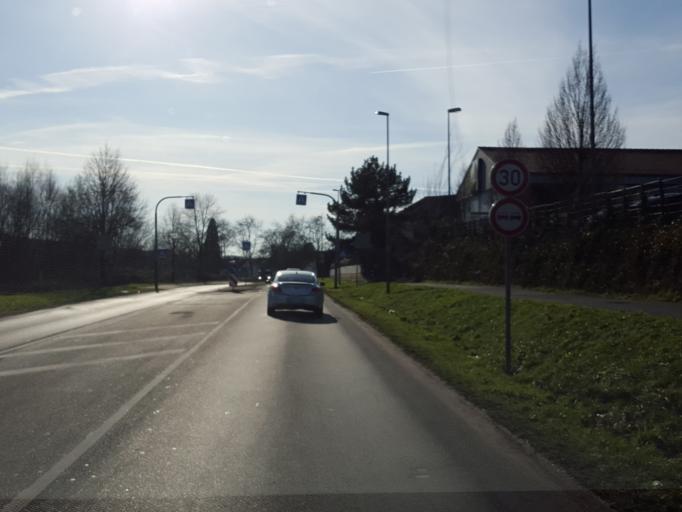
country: DE
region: Saarland
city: Volklingen
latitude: 49.2607
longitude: 6.8692
